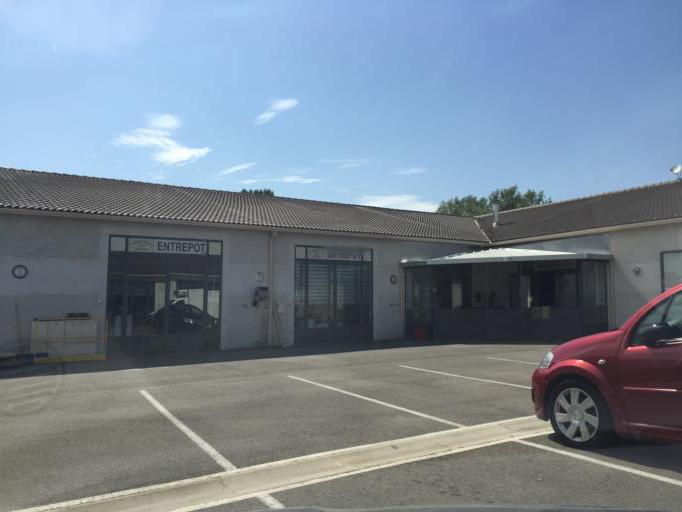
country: FR
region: Provence-Alpes-Cote d'Azur
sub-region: Departement du Vaucluse
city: Cavaillon
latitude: 43.8250
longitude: 5.0200
